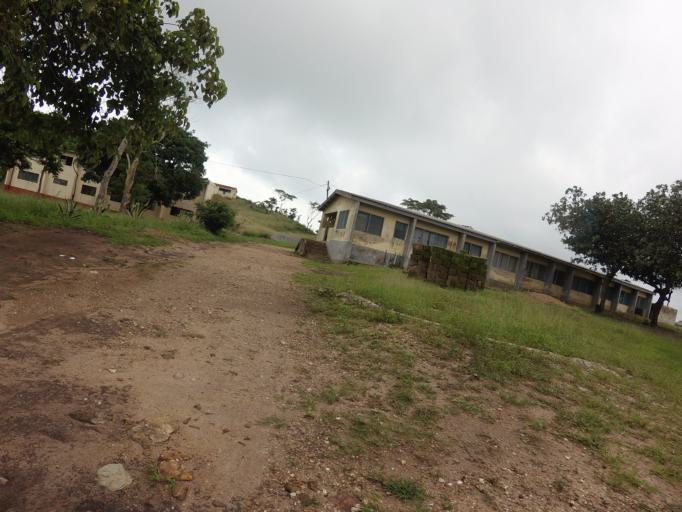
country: GH
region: Volta
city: Kpandu
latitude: 6.8512
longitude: 0.4354
